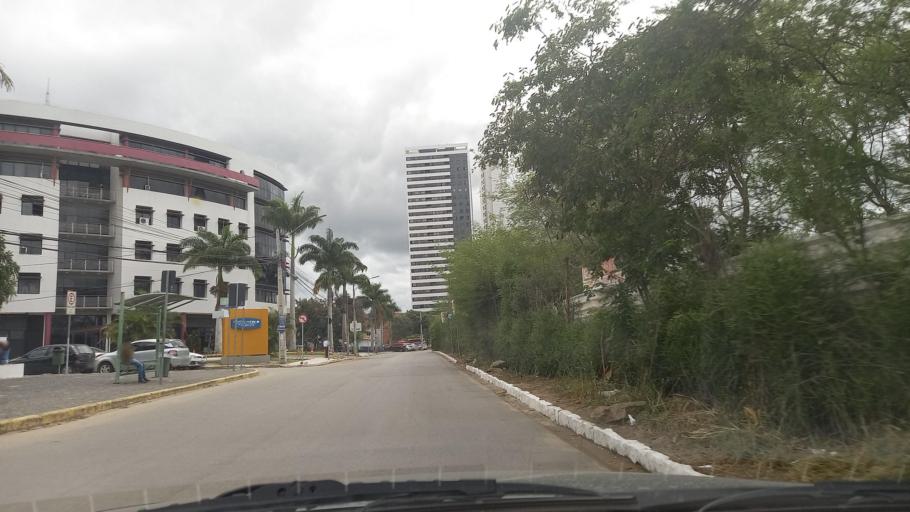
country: BR
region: Pernambuco
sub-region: Caruaru
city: Caruaru
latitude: -8.2604
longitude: -35.9659
